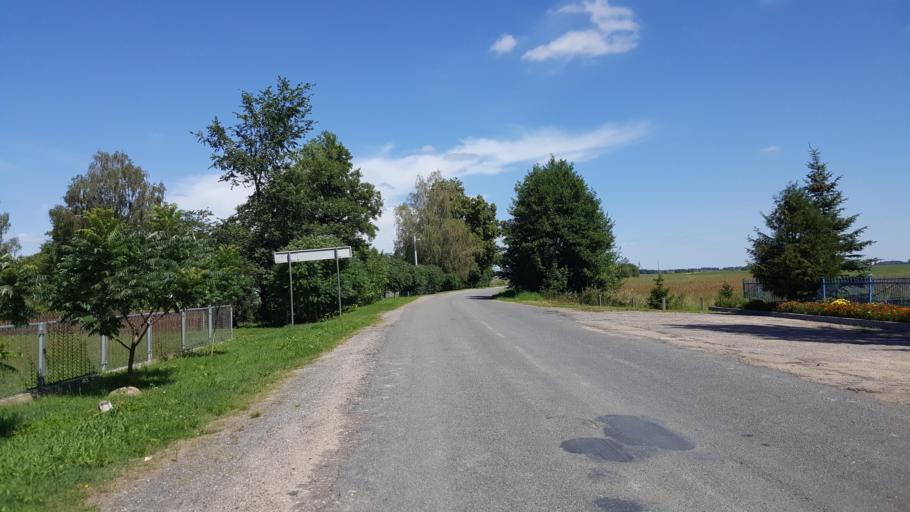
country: BY
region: Brest
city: Charnawchytsy
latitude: 52.3258
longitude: 23.6126
